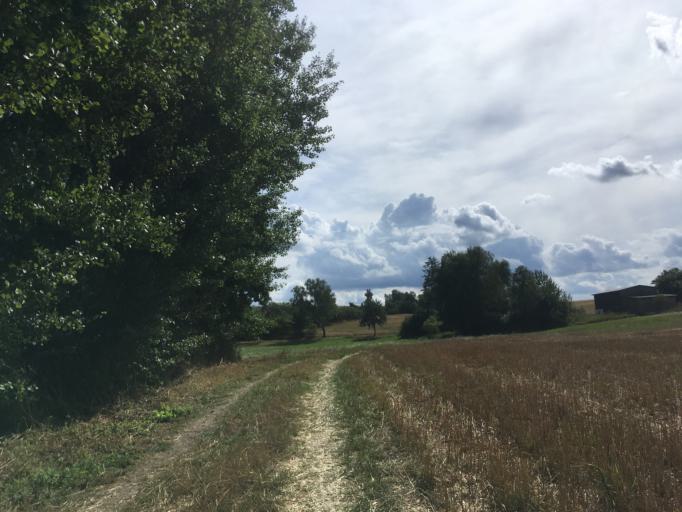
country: DE
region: Brandenburg
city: Gerswalde
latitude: 53.1289
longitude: 13.7876
